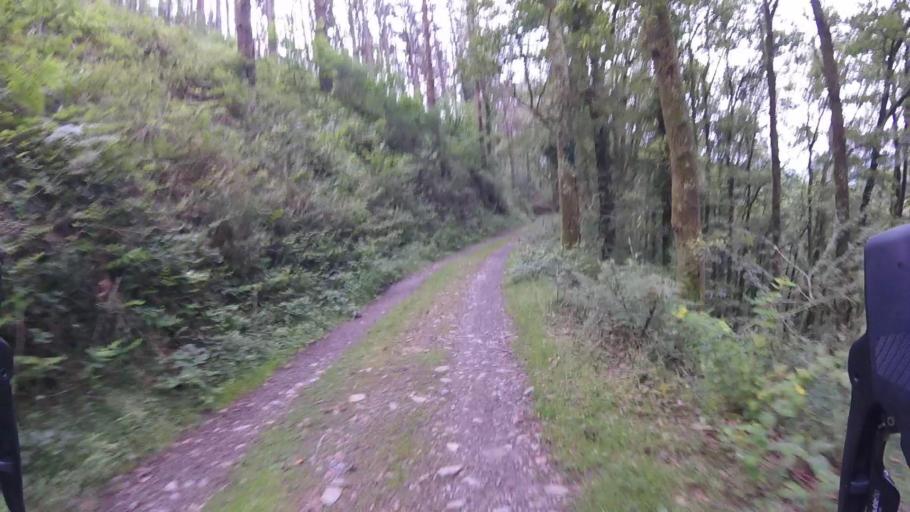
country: ES
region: Navarre
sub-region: Provincia de Navarra
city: Arano
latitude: 43.2512
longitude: -1.8662
